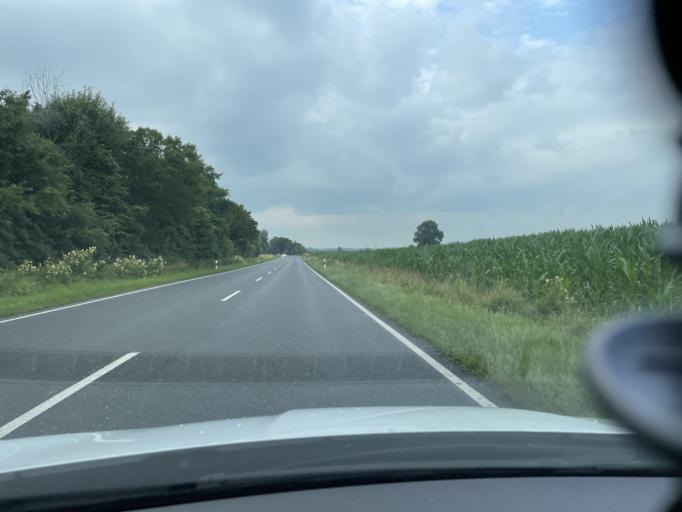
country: DE
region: Bavaria
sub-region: Upper Bavaria
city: Schechen
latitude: 47.9455
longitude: 12.1327
